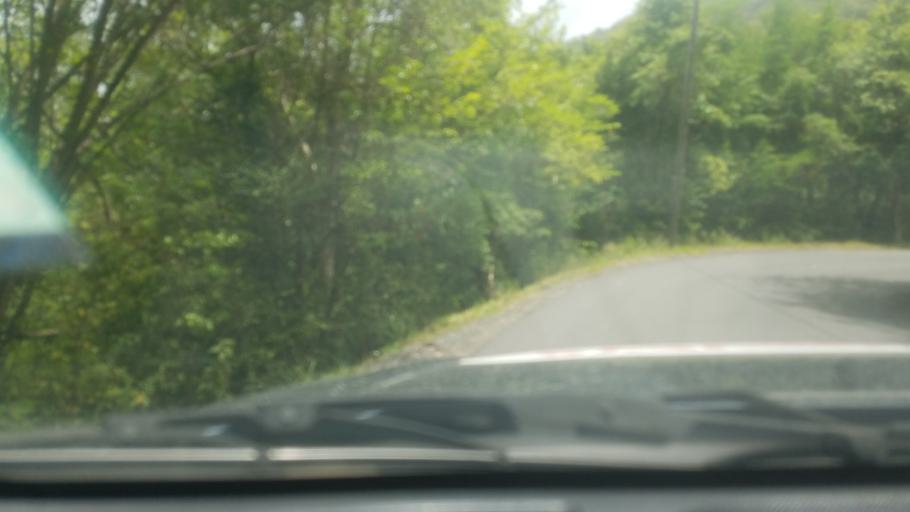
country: LC
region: Laborie Quarter
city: Laborie
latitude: 13.7577
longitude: -60.9873
